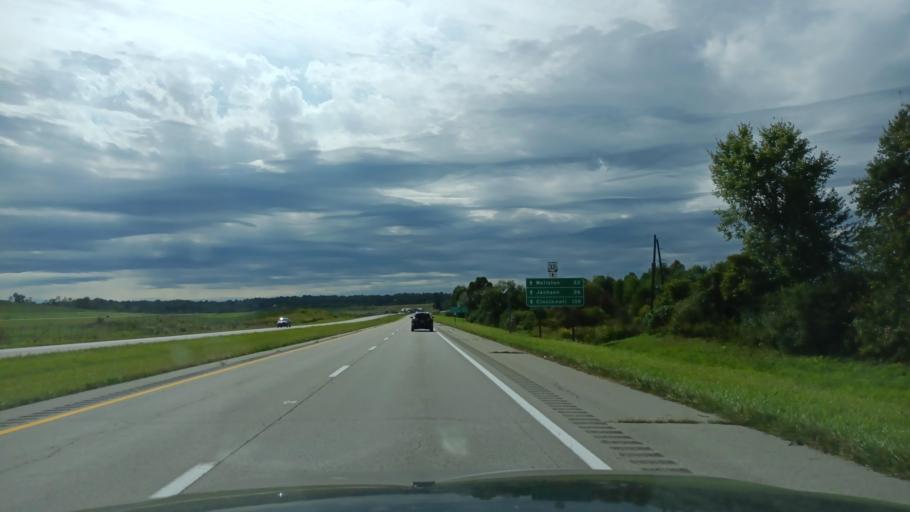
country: US
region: Ohio
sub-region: Athens County
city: Athens
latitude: 39.2131
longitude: -82.2304
